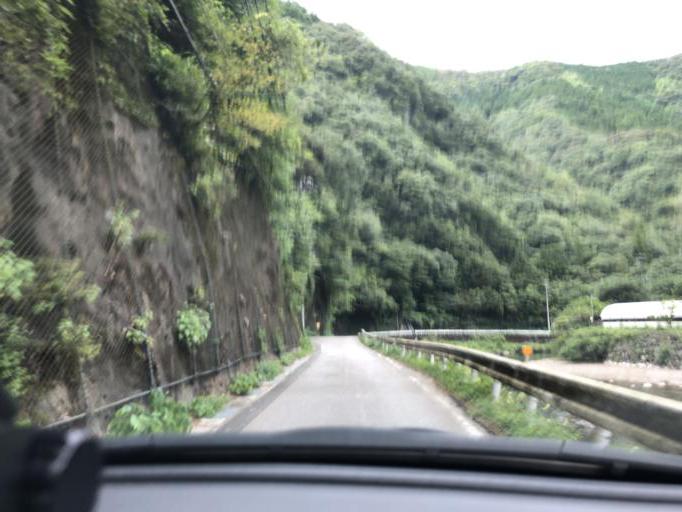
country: JP
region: Kochi
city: Kochi-shi
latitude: 33.6263
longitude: 133.5043
